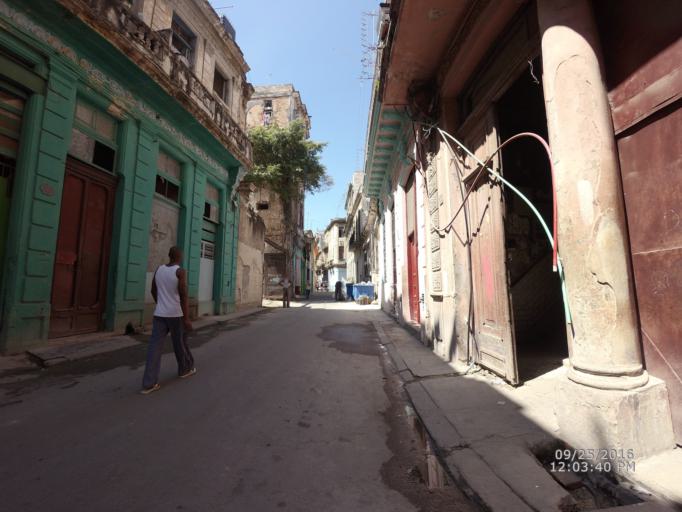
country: CU
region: La Habana
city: La Habana Vieja
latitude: 23.1375
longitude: -82.3554
